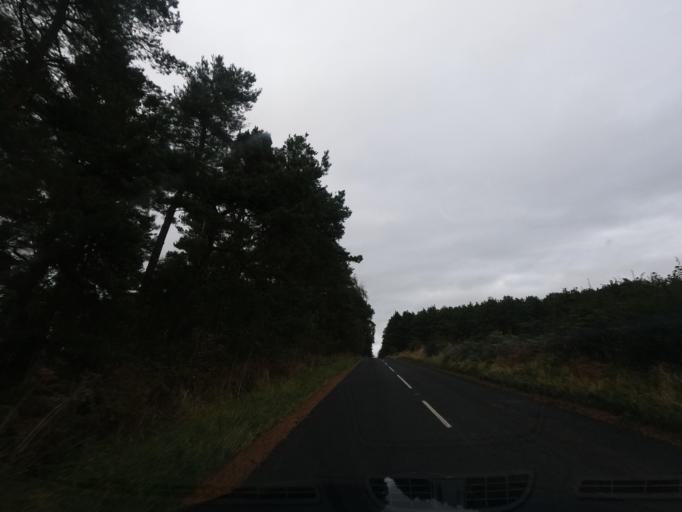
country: GB
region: England
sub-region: Northumberland
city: Doddington
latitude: 55.6003
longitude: -2.0020
